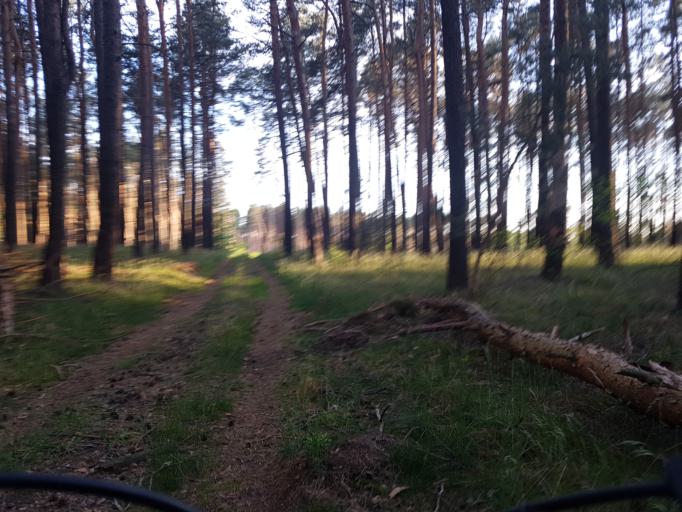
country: DE
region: Brandenburg
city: Schilda
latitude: 51.5623
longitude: 13.3767
